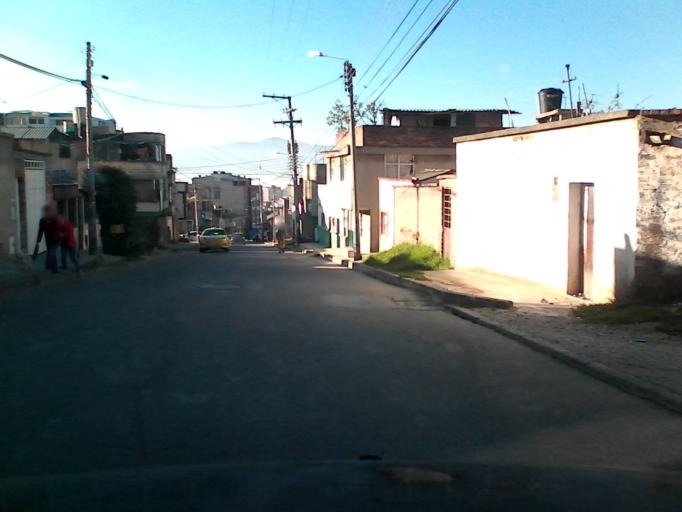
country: CO
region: Boyaca
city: Duitama
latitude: 5.8397
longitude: -73.0366
